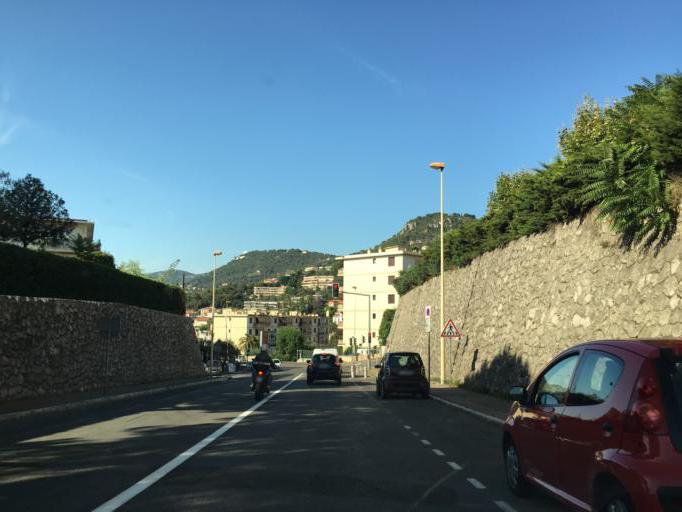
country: FR
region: Provence-Alpes-Cote d'Azur
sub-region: Departement des Alpes-Maritimes
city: Villefranche-sur-Mer
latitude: 43.7013
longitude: 7.2944
